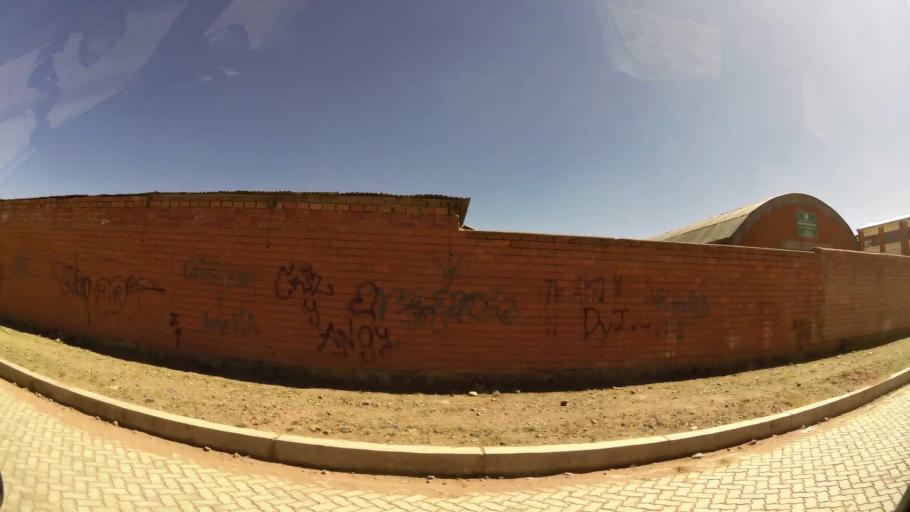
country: BO
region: La Paz
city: La Paz
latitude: -16.5379
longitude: -68.1950
